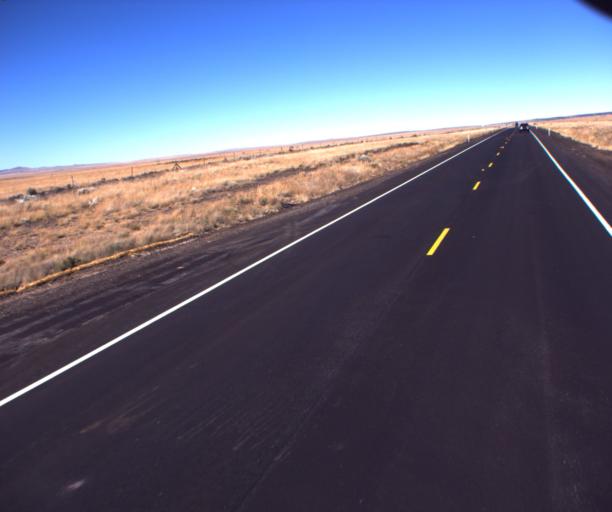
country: US
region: Arizona
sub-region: Apache County
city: Springerville
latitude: 34.2583
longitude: -109.3551
